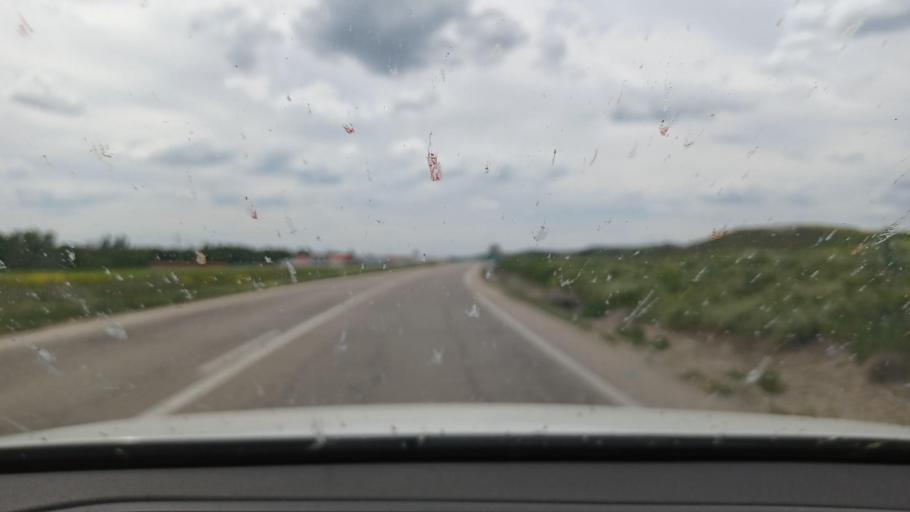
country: ES
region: Castille and Leon
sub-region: Provincia de Segovia
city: Cuellar
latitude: 41.3873
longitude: -4.2821
